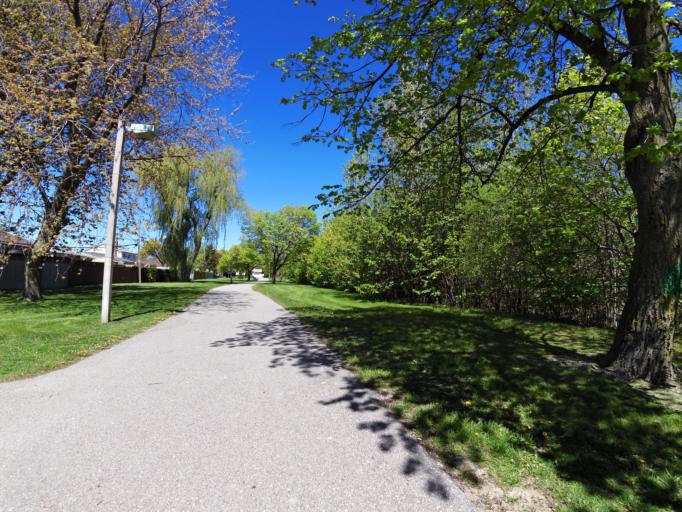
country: CA
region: Ontario
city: Brampton
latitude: 43.7116
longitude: -79.7074
